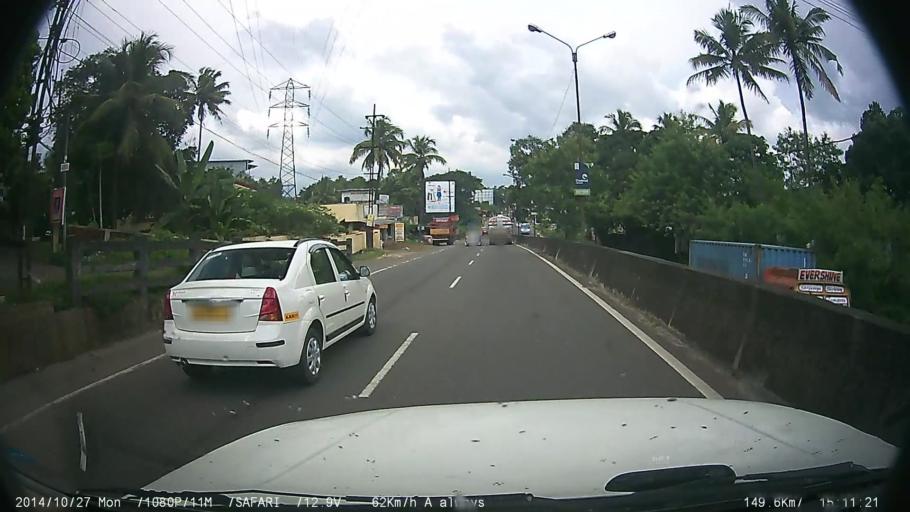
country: IN
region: Kerala
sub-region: Ernakulam
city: Aluva
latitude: 10.1275
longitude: 76.3423
